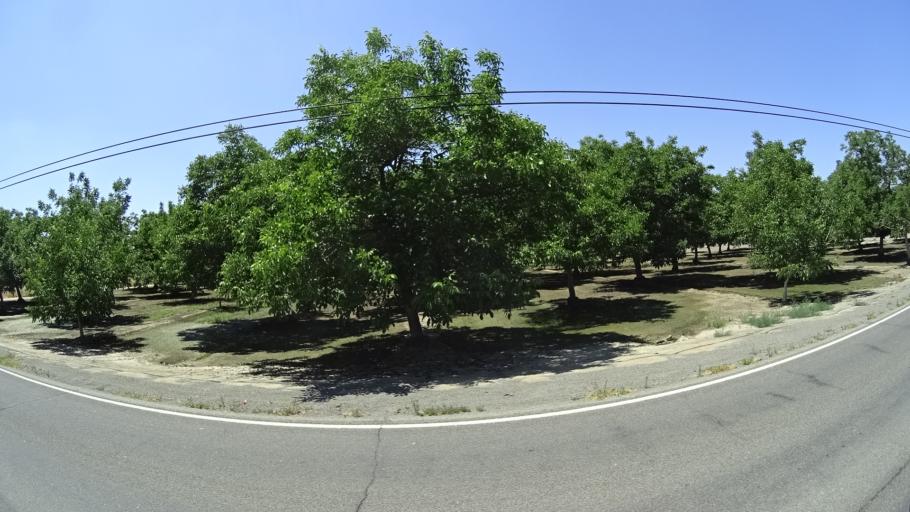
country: US
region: California
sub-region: Kings County
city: Lucerne
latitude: 36.3758
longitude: -119.6550
